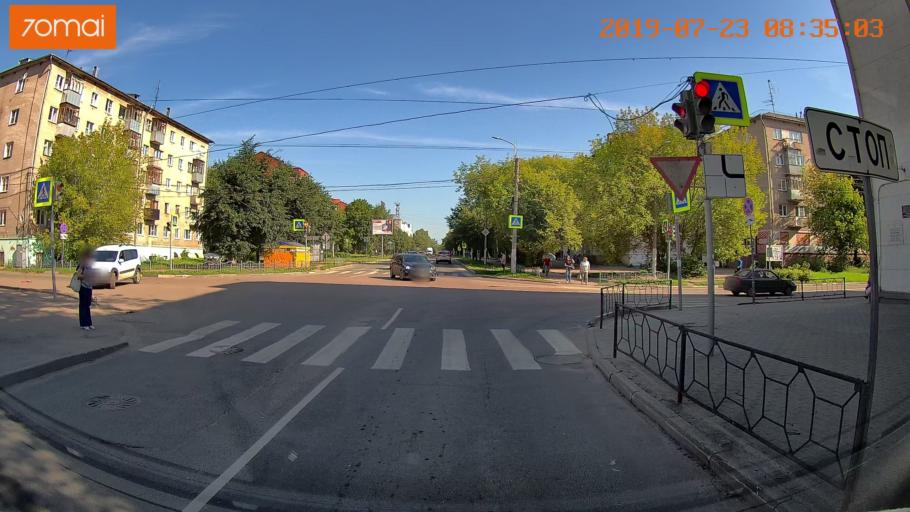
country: RU
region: Ivanovo
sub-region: Gorod Ivanovo
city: Ivanovo
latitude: 57.0055
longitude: 40.9805
